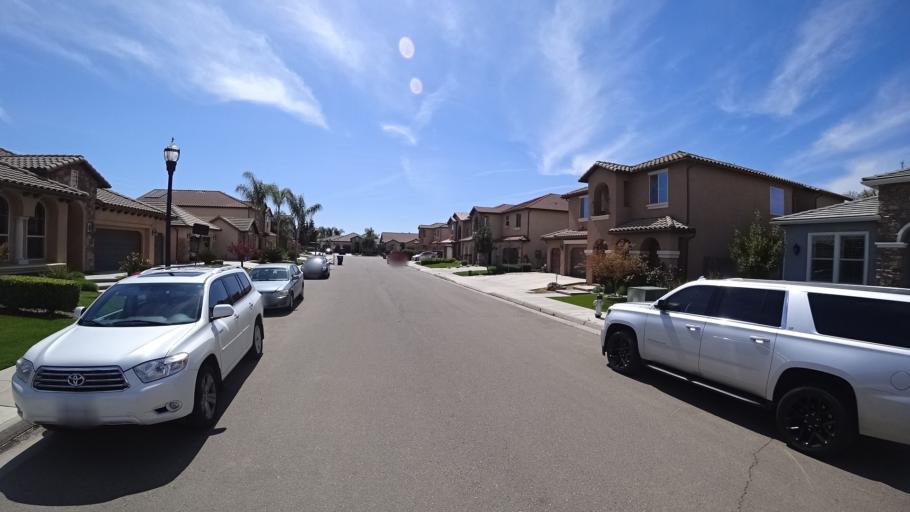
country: US
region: California
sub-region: Fresno County
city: Biola
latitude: 36.8253
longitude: -119.9149
